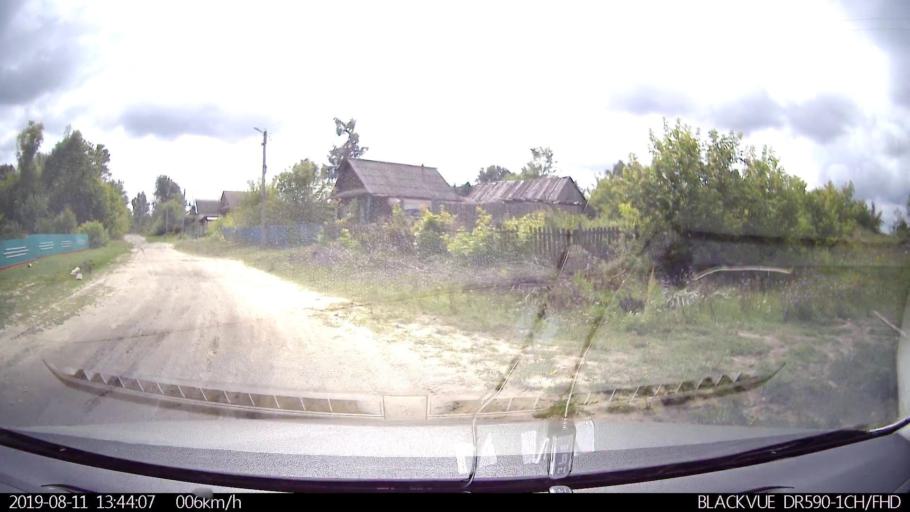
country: RU
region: Ulyanovsk
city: Ignatovka
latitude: 53.8536
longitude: 47.5744
